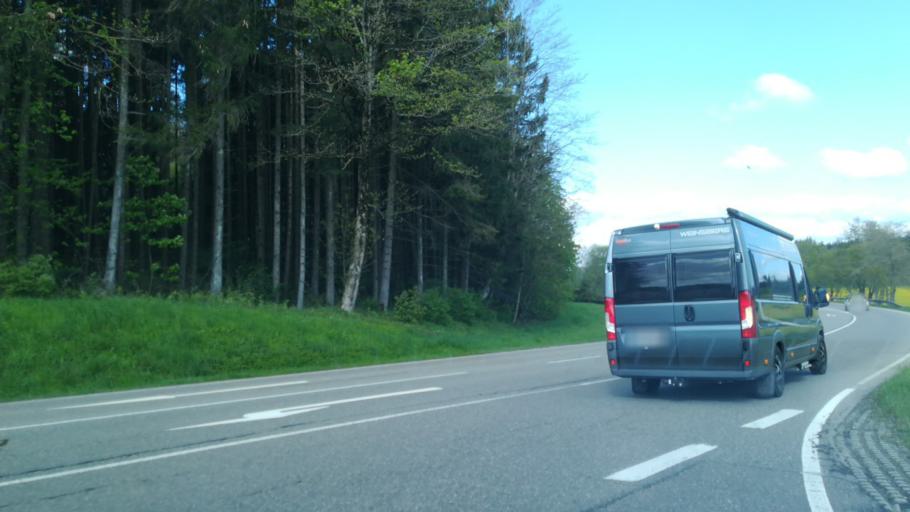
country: DE
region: Baden-Wuerttemberg
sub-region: Freiburg Region
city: Tengen
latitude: 47.8151
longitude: 8.5987
